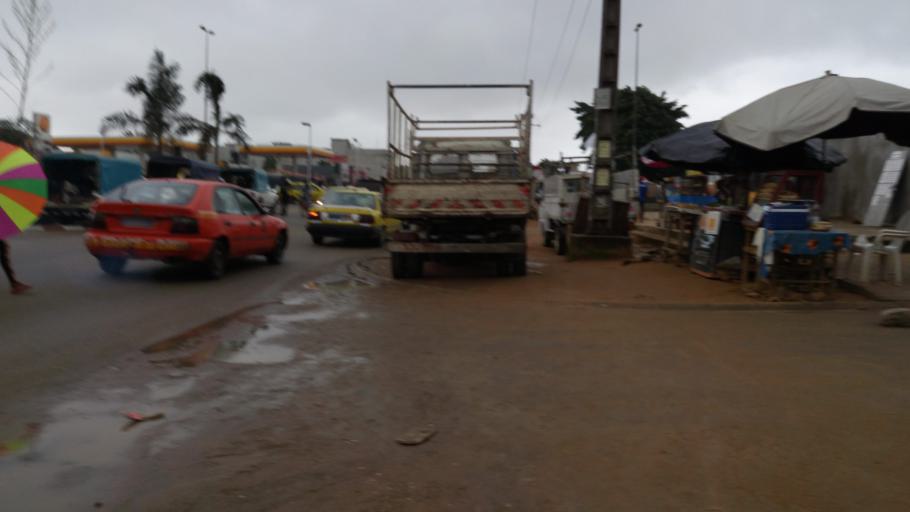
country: CI
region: Lagunes
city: Abobo
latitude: 5.4045
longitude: -3.9911
